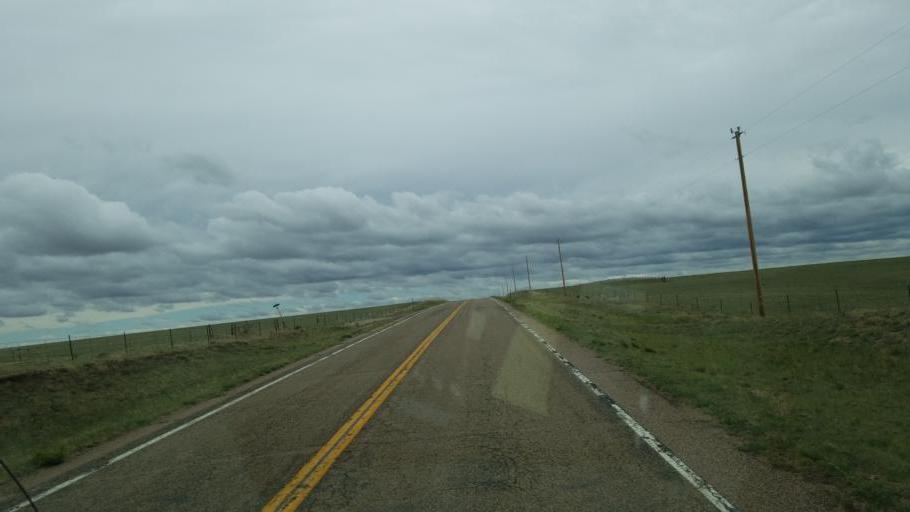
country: US
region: Colorado
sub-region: Lincoln County
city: Limon
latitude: 38.8382
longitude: -103.8586
